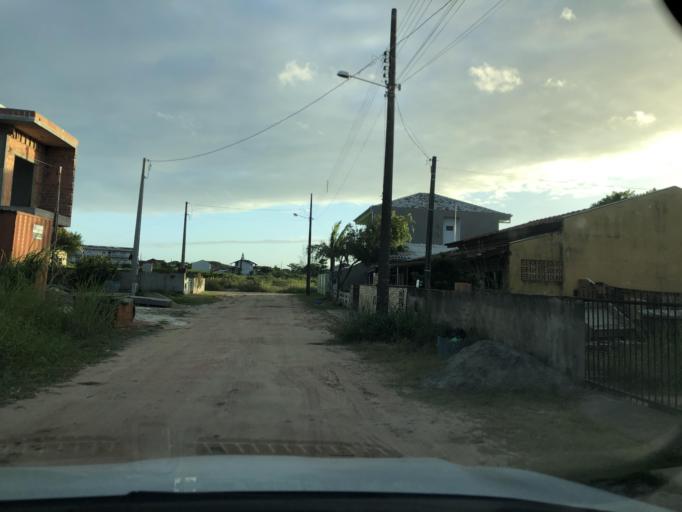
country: BR
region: Santa Catarina
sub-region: Sao Francisco Do Sul
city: Sao Francisco do Sul
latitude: -26.2350
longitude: -48.5078
